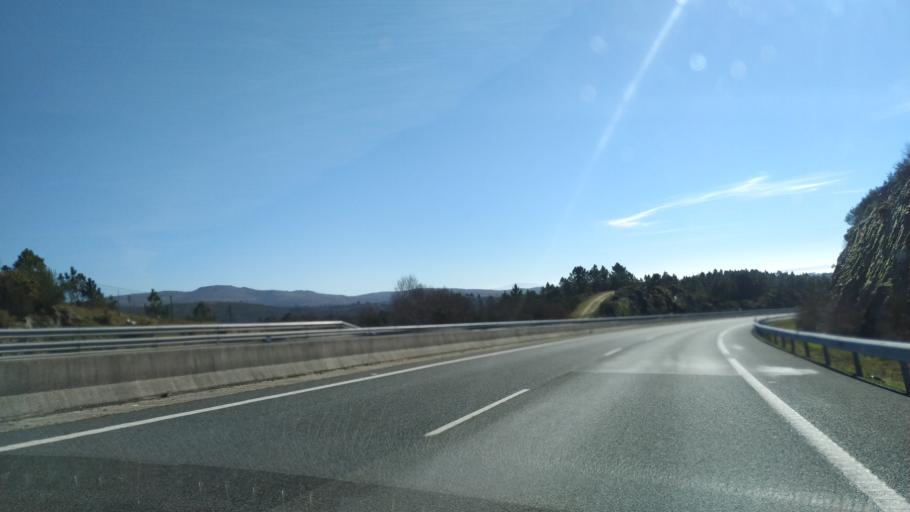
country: ES
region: Galicia
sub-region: Provincia de Ourense
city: Pinor
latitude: 42.5383
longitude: -8.0164
